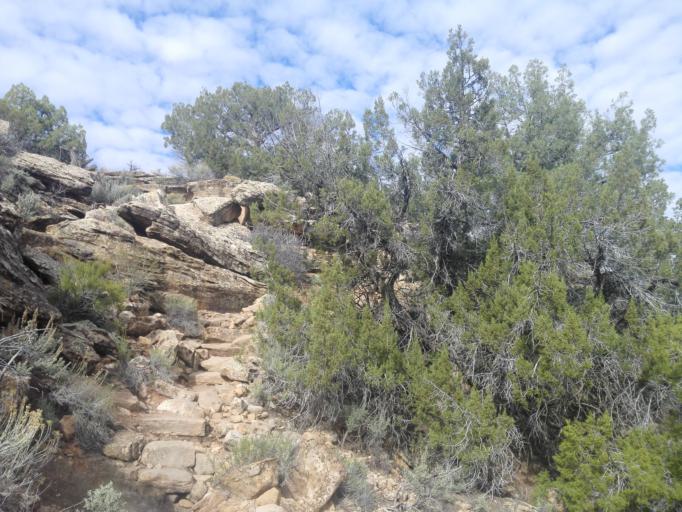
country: US
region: Colorado
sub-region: Montezuma County
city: Towaoc
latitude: 37.3823
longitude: -109.0757
